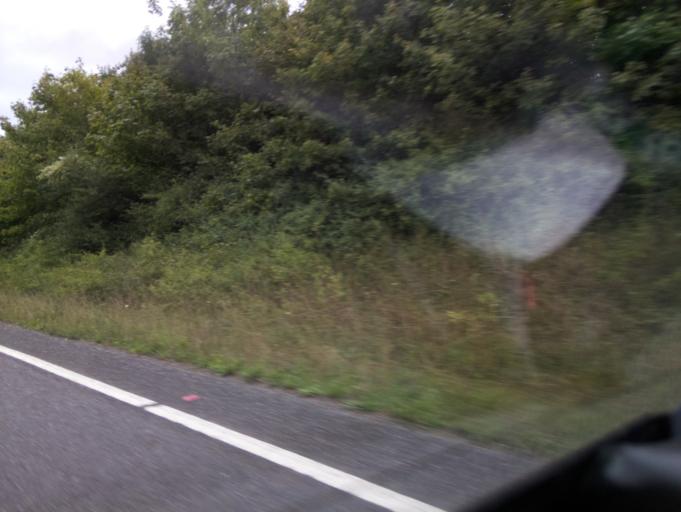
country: GB
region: England
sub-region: Devon
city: Marldon
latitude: 50.4543
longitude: -3.5901
